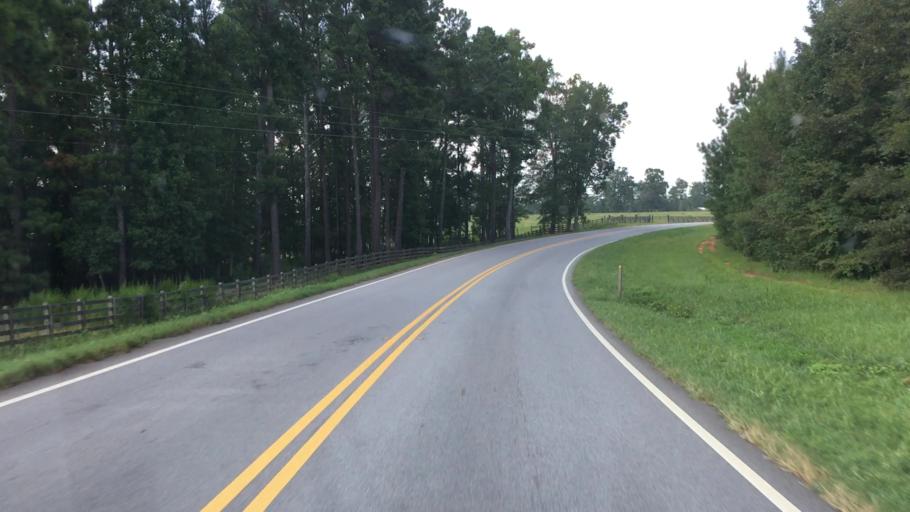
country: US
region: Georgia
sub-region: Jasper County
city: Monticello
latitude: 33.3728
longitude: -83.7550
